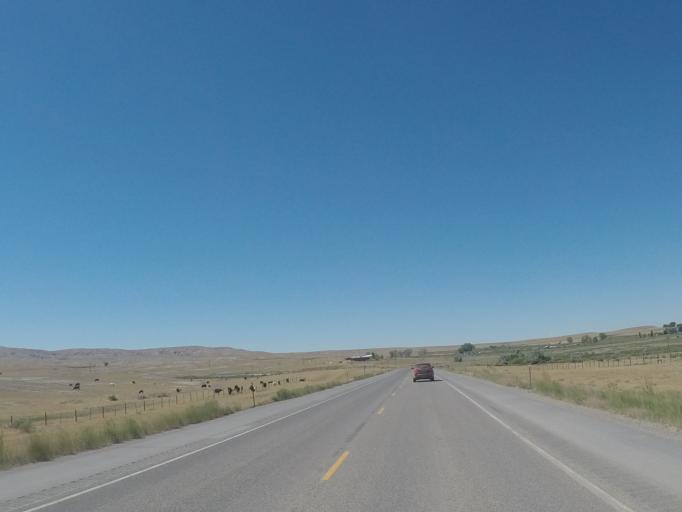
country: US
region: Wyoming
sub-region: Big Horn County
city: Greybull
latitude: 44.4980
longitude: -107.9759
